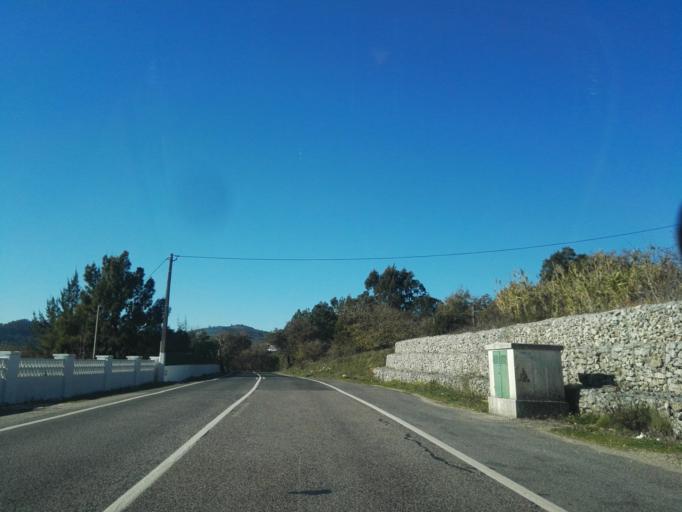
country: PT
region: Lisbon
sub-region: Mafra
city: Venda do Pinheiro
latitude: 38.9143
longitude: -9.2122
